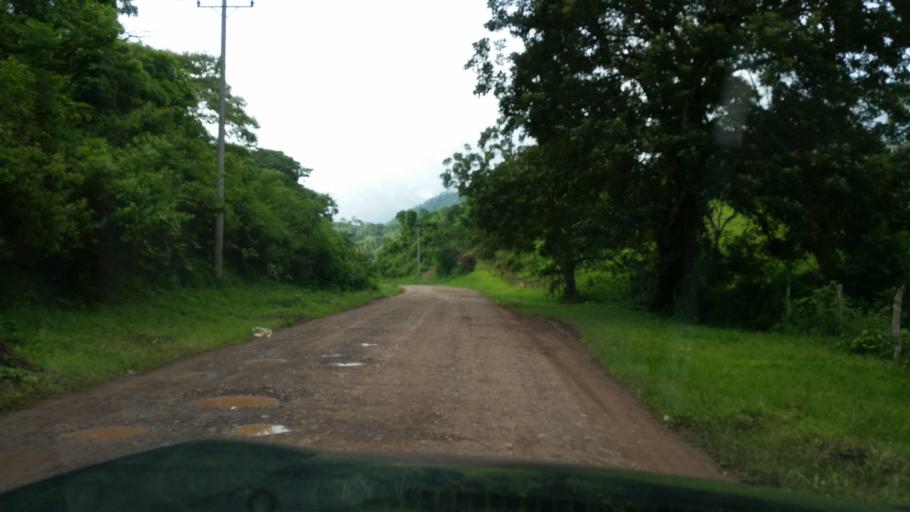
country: NI
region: Jinotega
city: Jinotega
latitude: 13.2289
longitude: -85.7290
